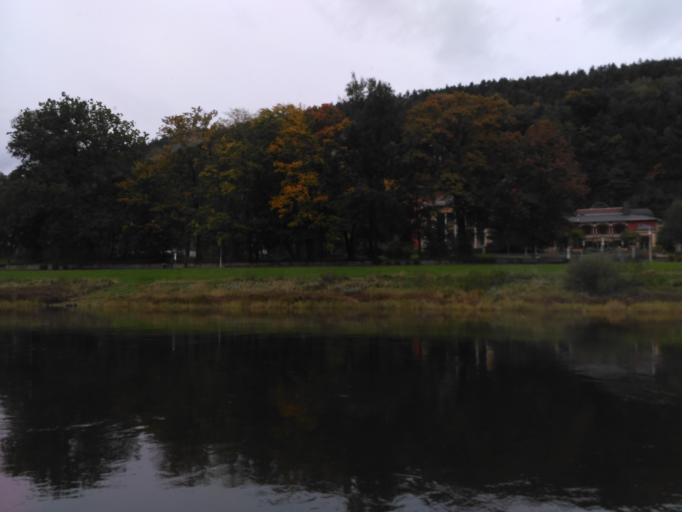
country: DE
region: Saxony
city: Bad Schandau
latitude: 50.9145
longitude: 14.1610
